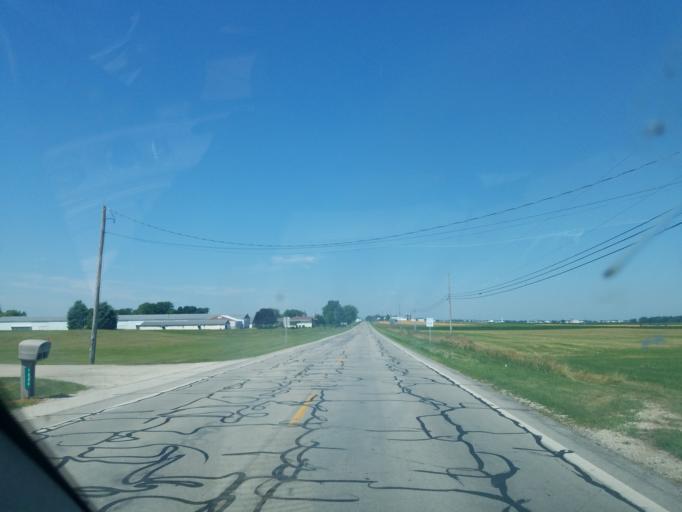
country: US
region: Ohio
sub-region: Auglaize County
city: New Bremen
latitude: 40.4077
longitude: -84.4981
